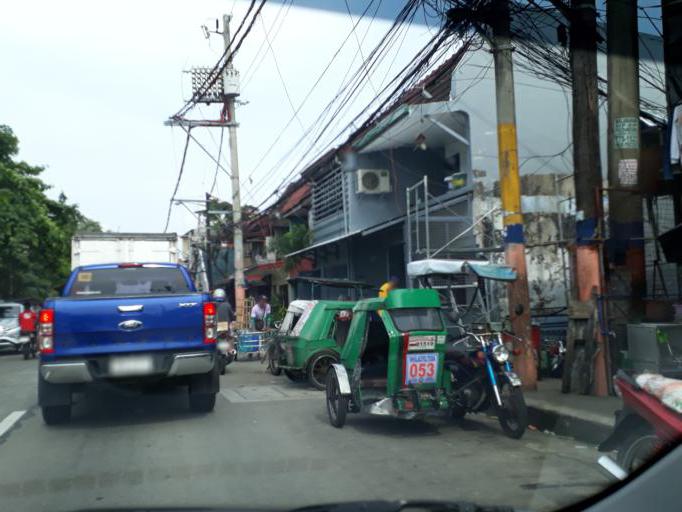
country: PH
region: Metro Manila
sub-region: City of Manila
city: Manila
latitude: 14.6222
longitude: 120.9851
